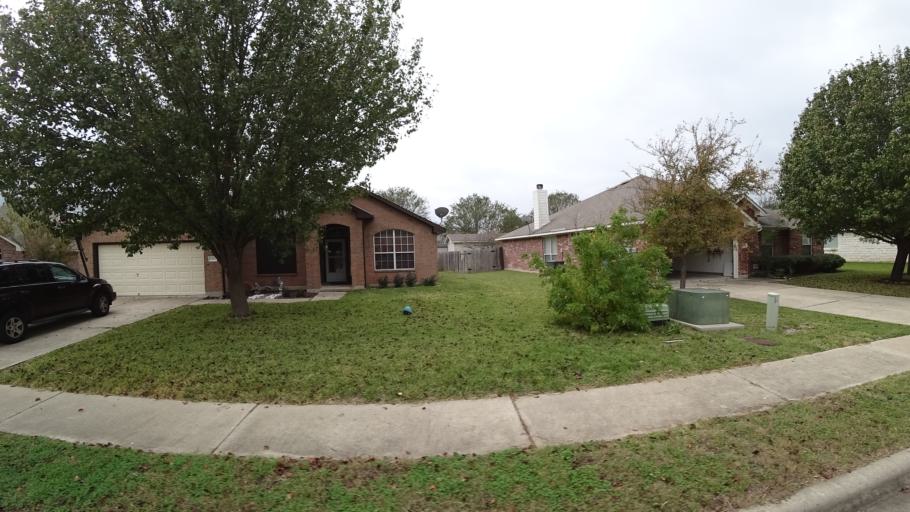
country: US
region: Texas
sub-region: Travis County
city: Pflugerville
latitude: 30.4375
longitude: -97.6041
